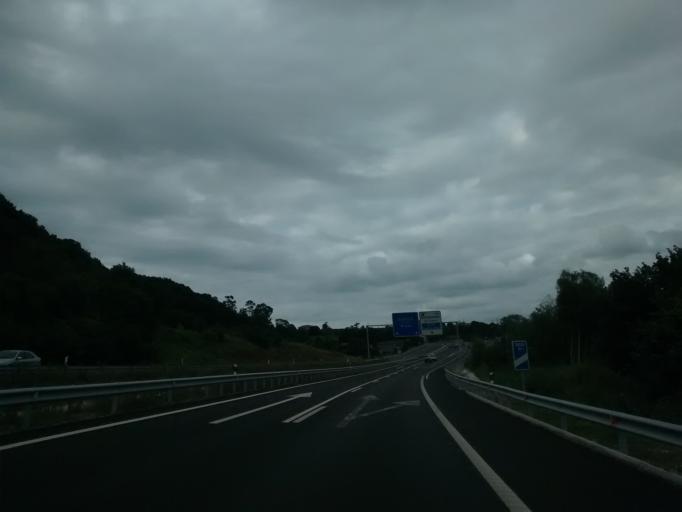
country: ES
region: Cantabria
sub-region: Provincia de Cantabria
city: Lierganes
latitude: 43.3821
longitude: -3.7470
